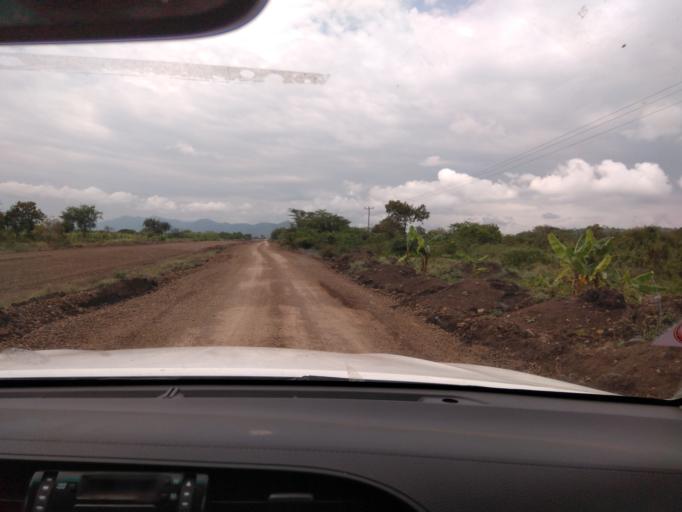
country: ET
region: Southern Nations, Nationalities, and People's Region
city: Felege Neway
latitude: 6.4072
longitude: 37.1375
